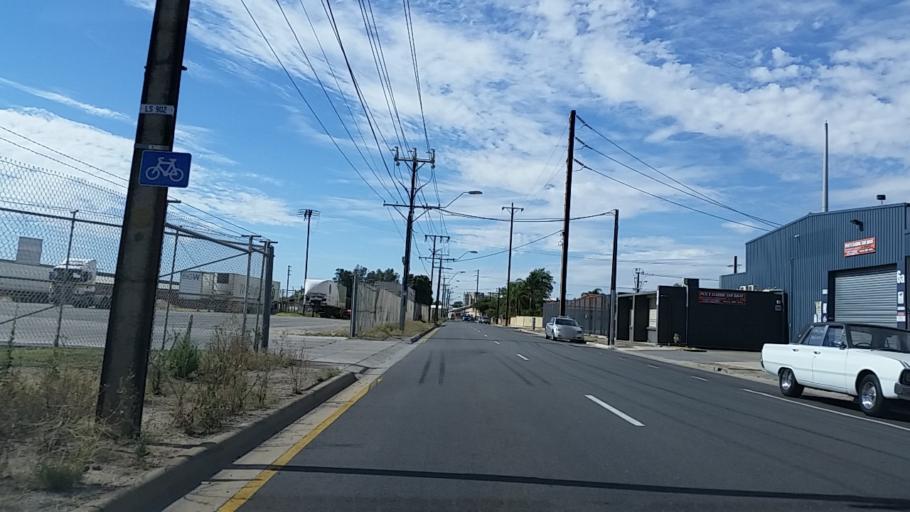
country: AU
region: South Australia
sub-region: Port Adelaide Enfield
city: Alberton
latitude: -34.8538
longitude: 138.5380
